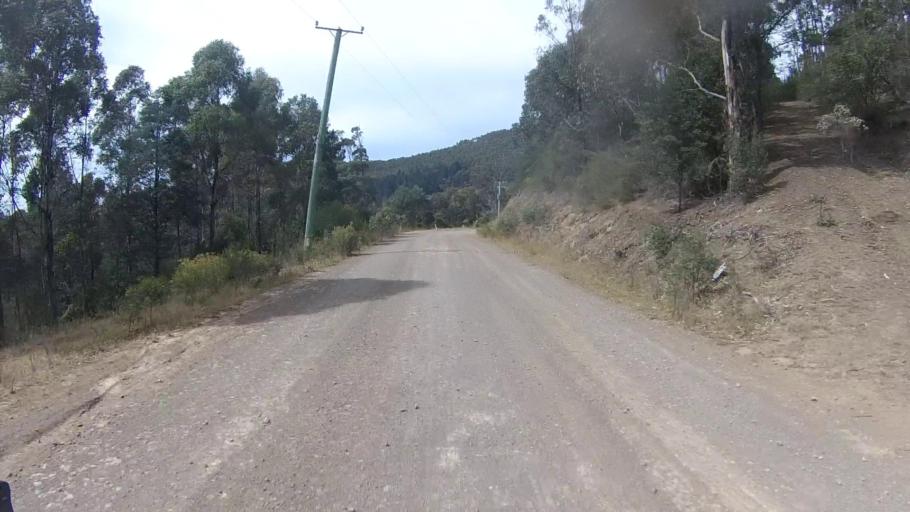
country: AU
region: Tasmania
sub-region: Sorell
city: Sorell
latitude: -42.7727
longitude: 147.8301
